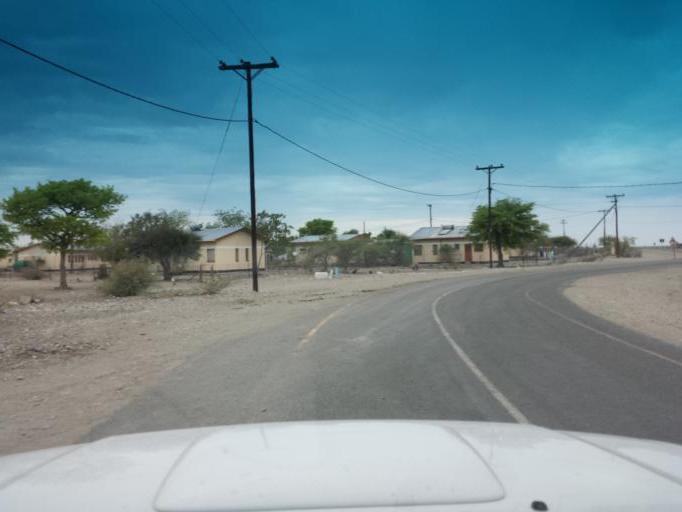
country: BW
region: Central
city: Mopipi
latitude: -21.2029
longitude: 24.8567
